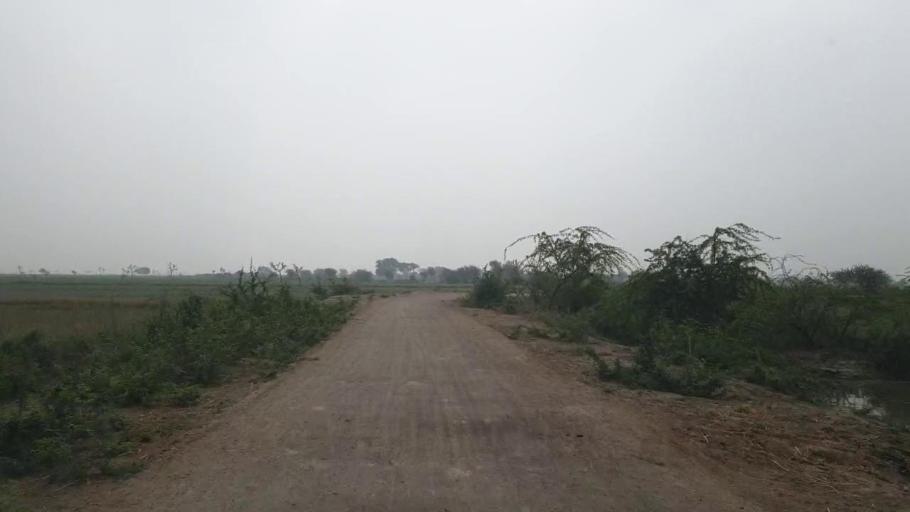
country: PK
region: Sindh
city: Badin
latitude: 24.5761
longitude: 68.6853
